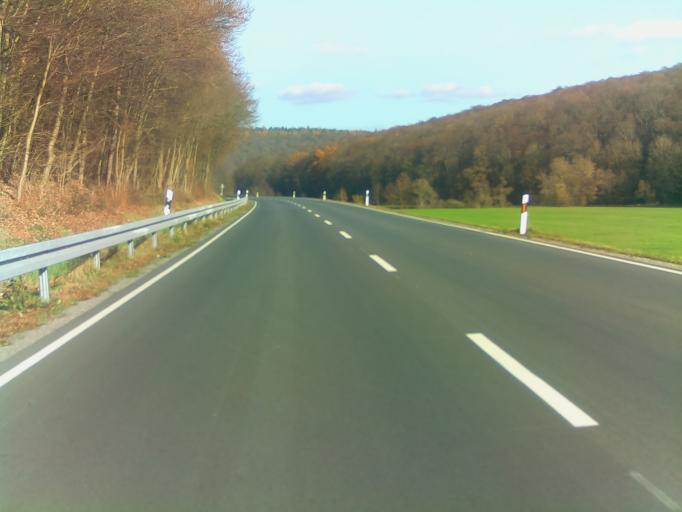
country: DE
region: Bavaria
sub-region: Regierungsbezirk Unterfranken
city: Euerdorf
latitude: 50.1605
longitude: 10.0386
